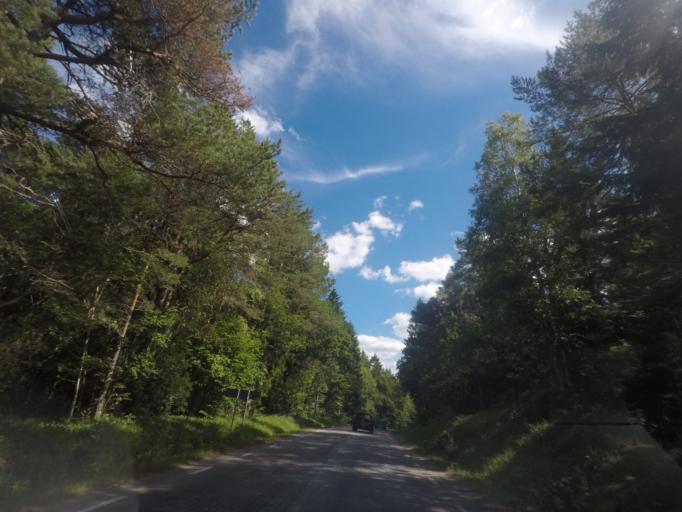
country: SE
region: Stockholm
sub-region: Norrtalje Kommun
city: Arno
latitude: 60.1204
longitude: 18.7873
